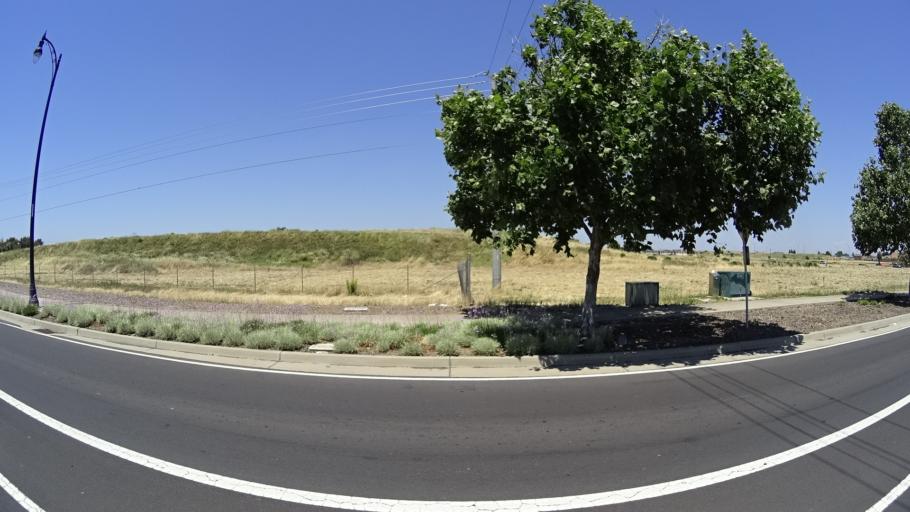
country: US
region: California
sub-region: Sacramento County
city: Laguna
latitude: 38.4381
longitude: -121.3991
